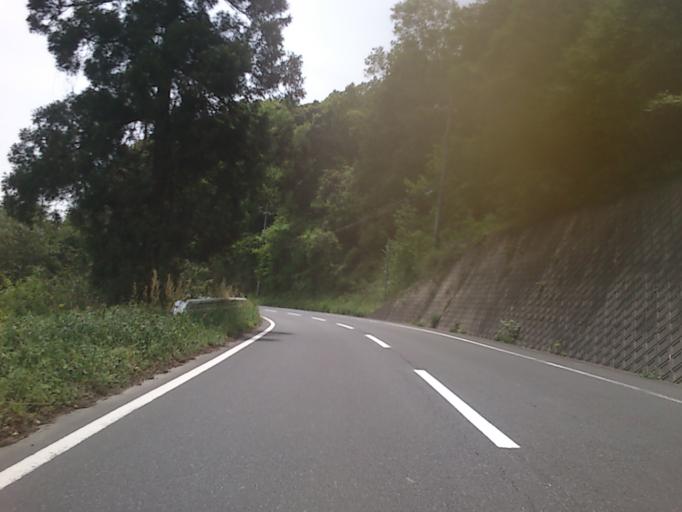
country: JP
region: Kyoto
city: Miyazu
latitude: 35.6491
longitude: 135.0852
